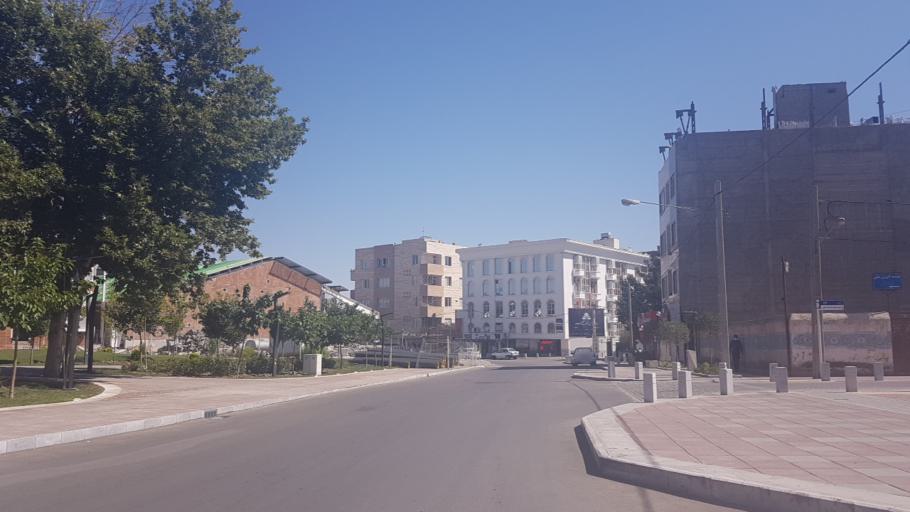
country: IR
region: Razavi Khorasan
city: Mashhad
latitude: 36.3103
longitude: 59.5132
